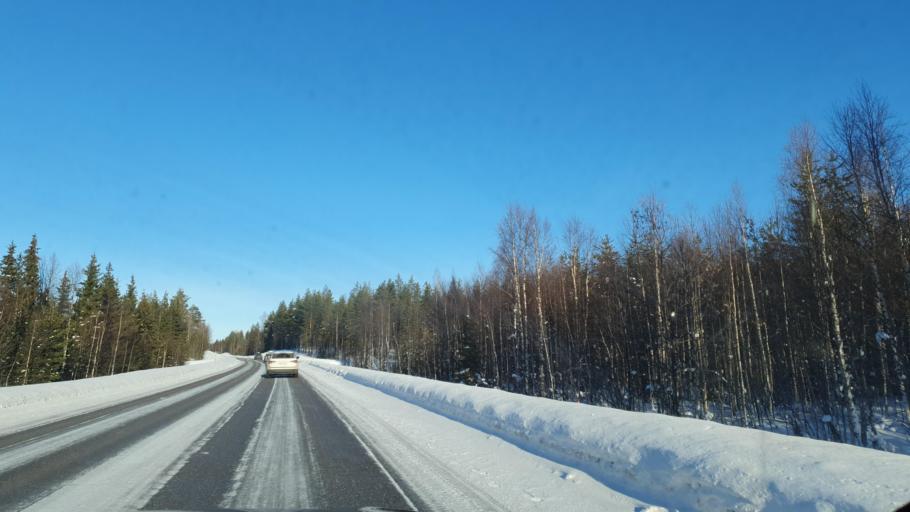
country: FI
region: Lapland
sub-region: Torniolaakso
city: Pello
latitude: 66.8760
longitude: 24.0626
